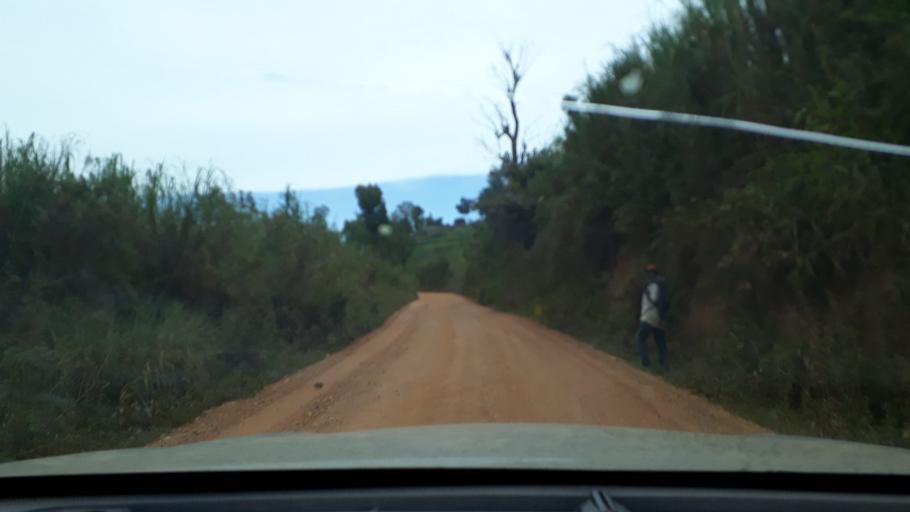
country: CD
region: Eastern Province
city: Bunia
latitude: 1.8510
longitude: 30.4768
